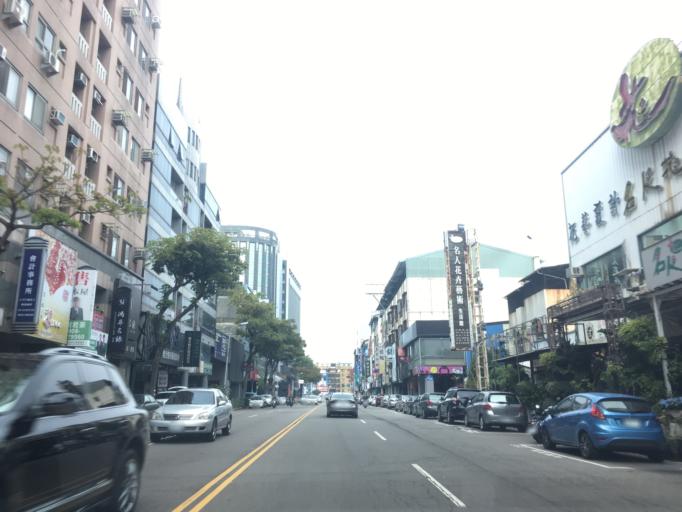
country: TW
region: Taiwan
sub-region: Taichung City
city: Taichung
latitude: 24.1569
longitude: 120.6546
